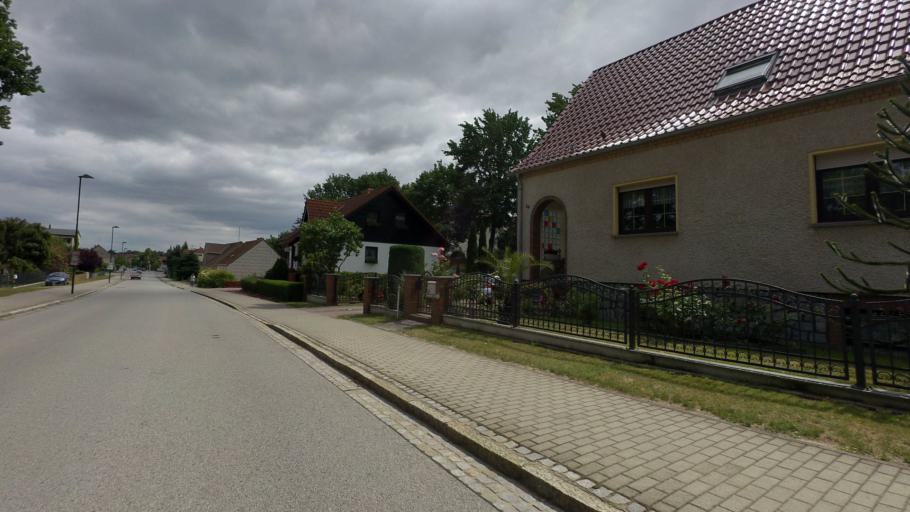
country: DE
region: Brandenburg
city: Luckau
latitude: 51.8510
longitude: 13.6995
